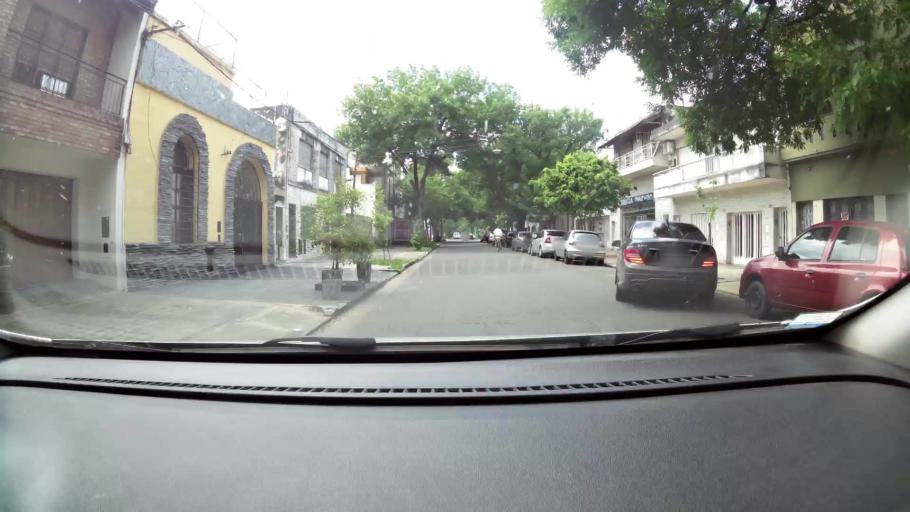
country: AR
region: Santa Fe
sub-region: Departamento de Rosario
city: Rosario
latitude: -32.9662
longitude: -60.6442
